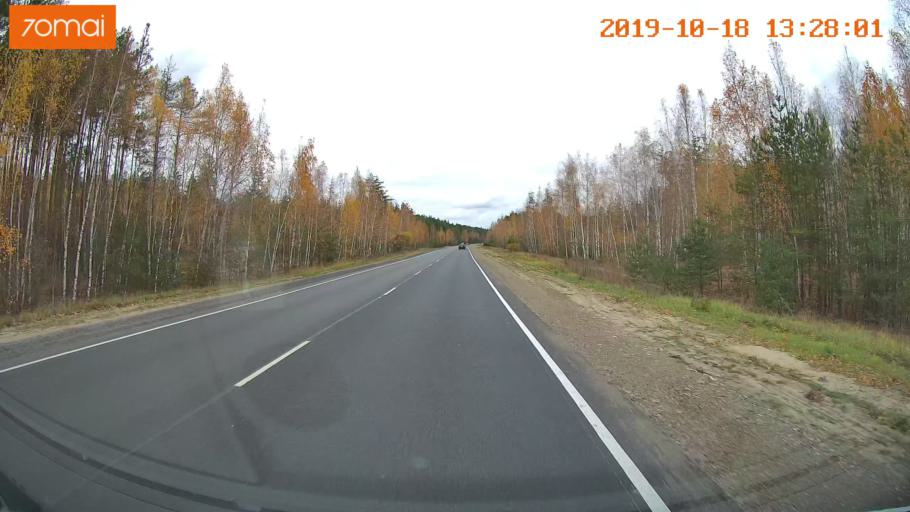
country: RU
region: Rjazan
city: Solotcha
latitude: 54.7730
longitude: 39.8607
